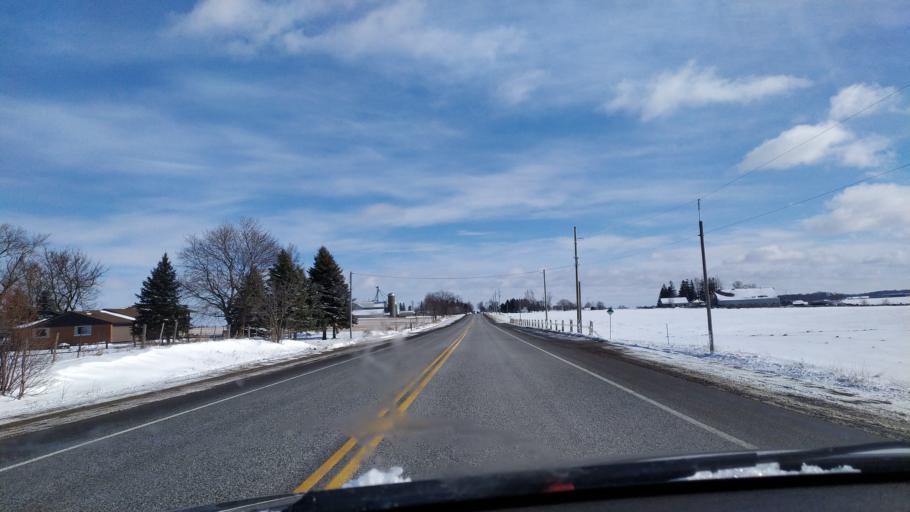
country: CA
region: Ontario
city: Waterloo
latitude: 43.5246
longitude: -80.6710
